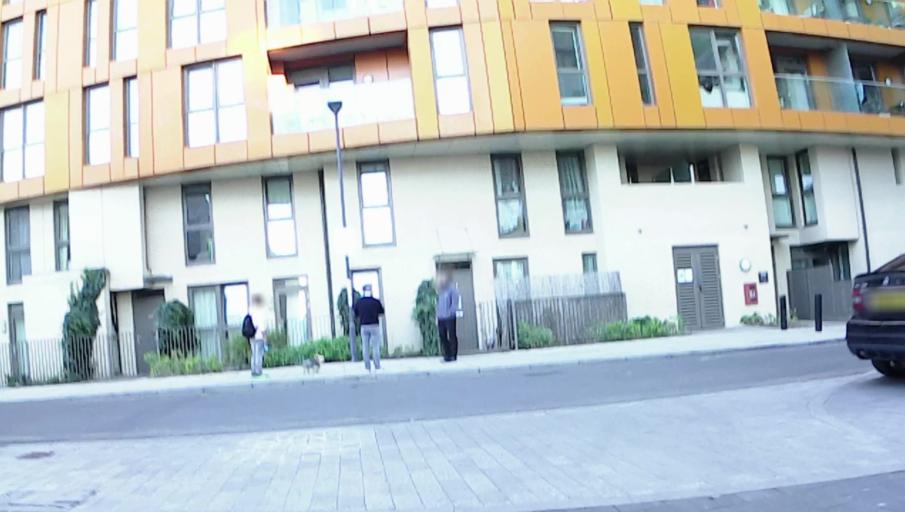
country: GB
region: England
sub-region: Greater London
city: Blackheath
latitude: 51.4898
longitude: 0.0051
